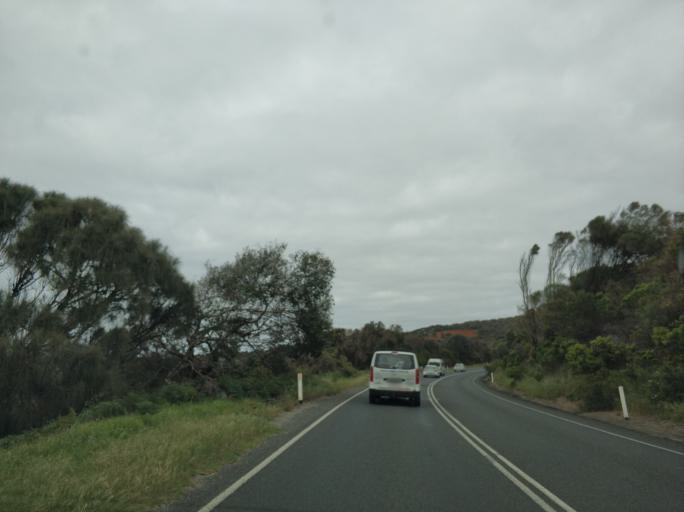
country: AU
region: Victoria
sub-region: Surf Coast
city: Anglesea
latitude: -38.4334
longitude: 144.1331
